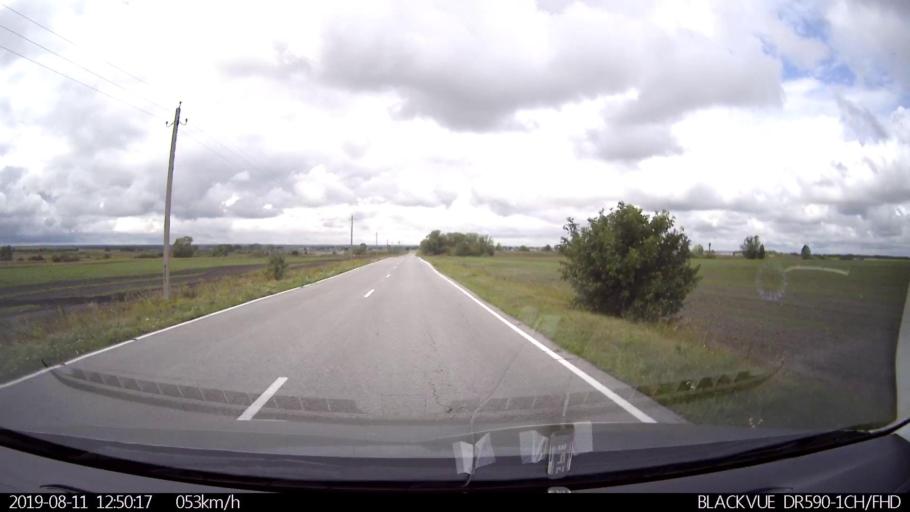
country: RU
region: Ulyanovsk
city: Ignatovka
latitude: 53.8751
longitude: 47.6749
